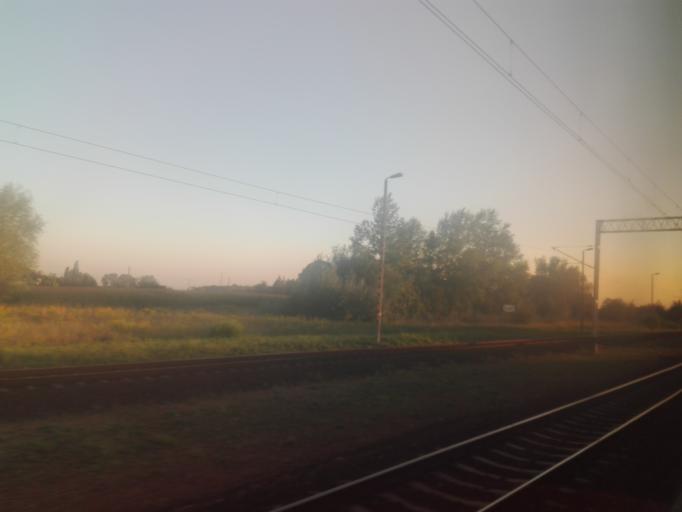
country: PL
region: Masovian Voivodeship
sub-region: Powiat warszawski zachodni
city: Blonie
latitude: 52.1866
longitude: 20.6031
